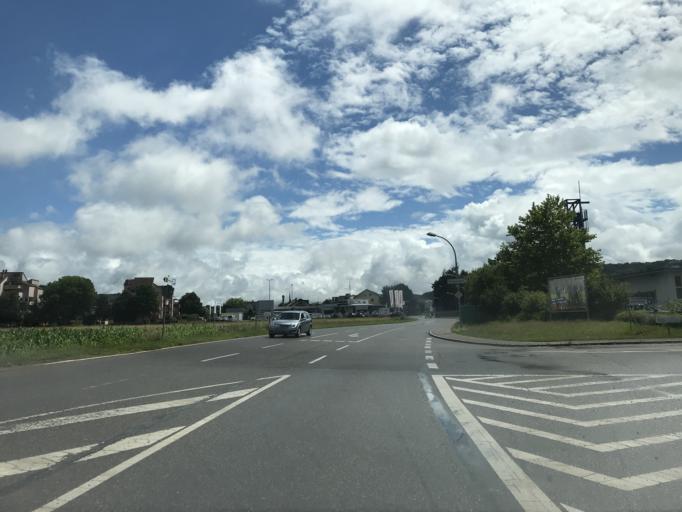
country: DE
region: Baden-Wuerttemberg
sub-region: Freiburg Region
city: Steinen
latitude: 47.6432
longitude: 7.7283
